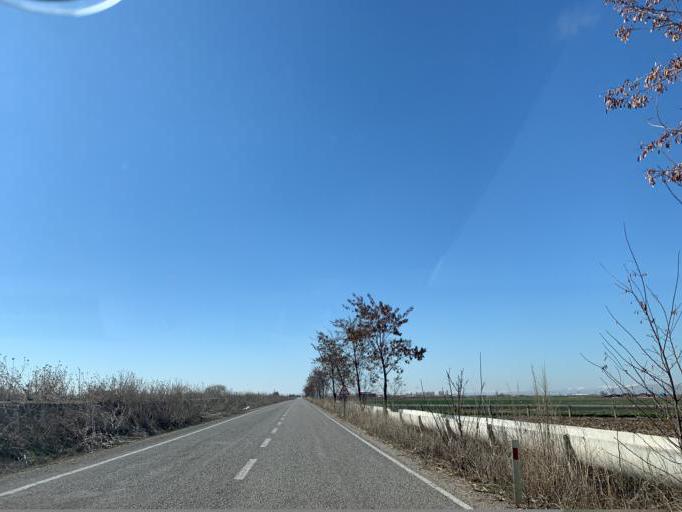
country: TR
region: Konya
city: Catalhoeyuek
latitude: 37.6218
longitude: 32.8026
